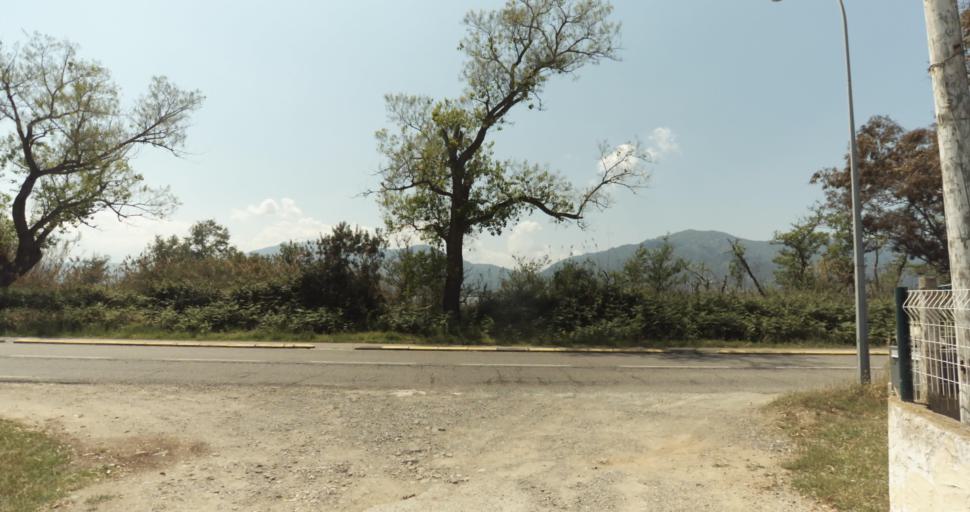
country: FR
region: Corsica
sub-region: Departement de la Haute-Corse
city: Biguglia
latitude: 42.6261
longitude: 9.4692
